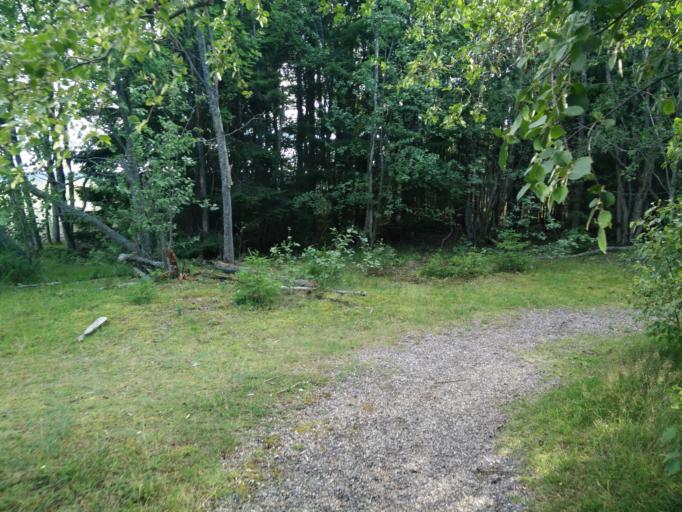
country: SE
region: Vaesternorrland
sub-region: Timra Kommun
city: Soraker
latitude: 62.4497
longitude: 17.4971
